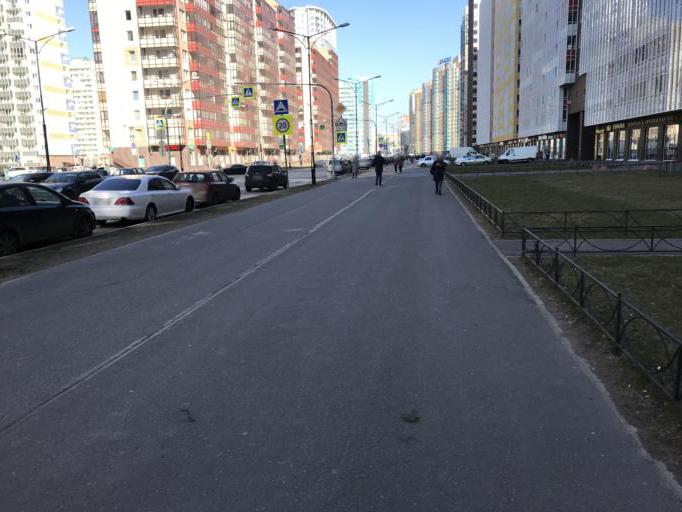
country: RU
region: Leningrad
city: Rybatskoye
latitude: 59.9002
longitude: 30.5116
